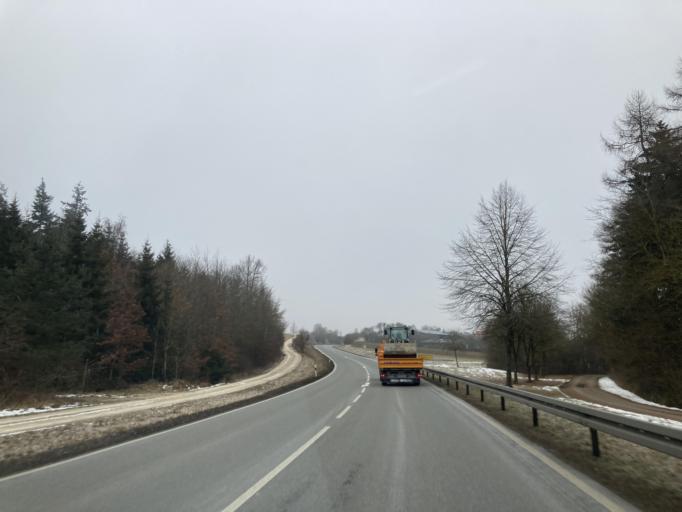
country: DE
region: Baden-Wuerttemberg
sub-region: Freiburg Region
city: Buchheim
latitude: 47.9834
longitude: 8.9801
